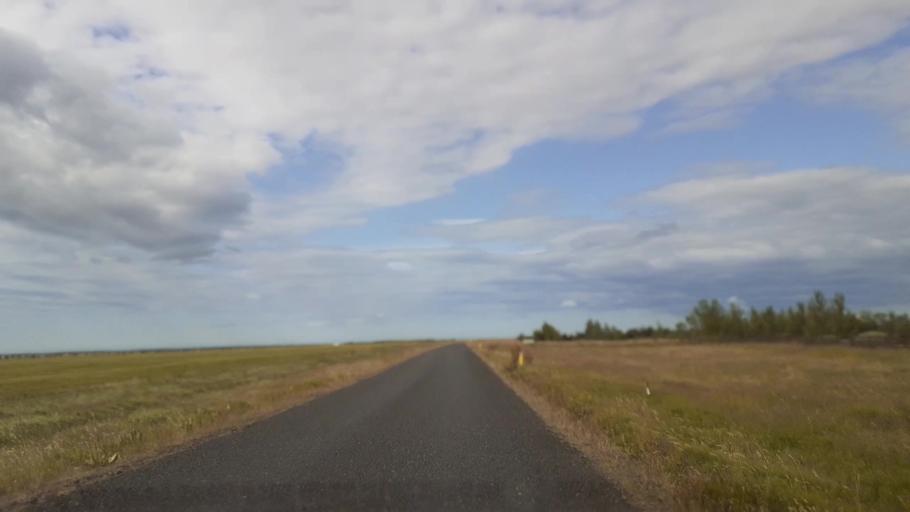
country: IS
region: South
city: Vestmannaeyjar
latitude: 63.7695
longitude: -20.2948
